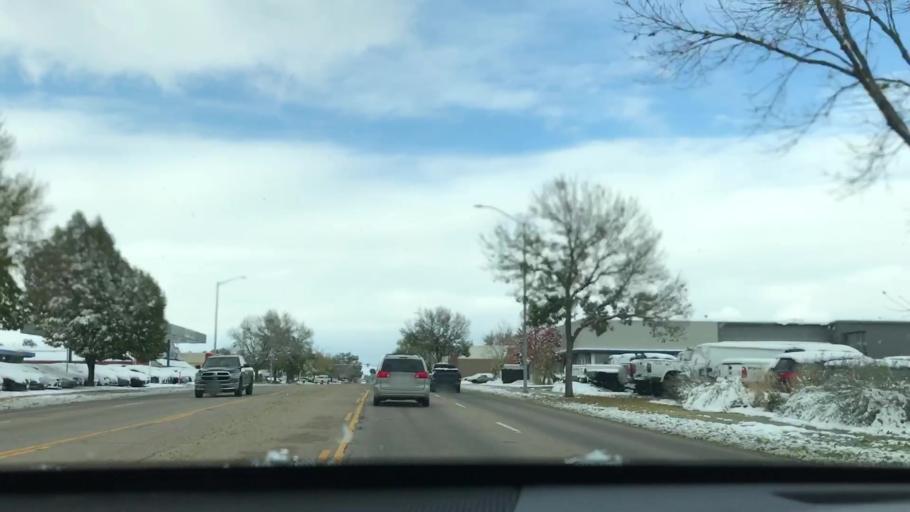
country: US
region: Colorado
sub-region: Boulder County
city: Longmont
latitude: 40.1819
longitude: -105.1024
